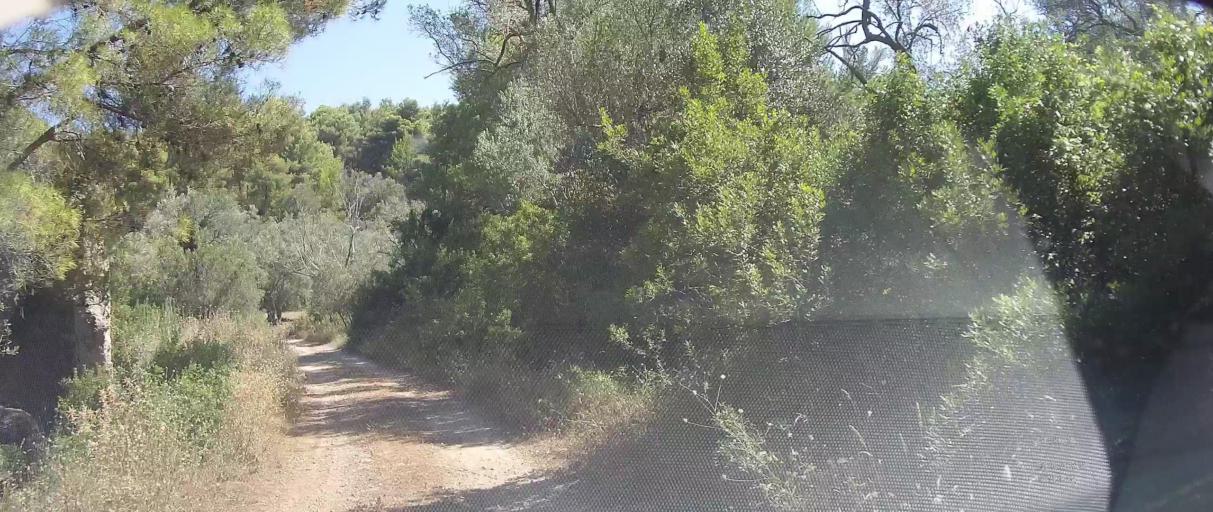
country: HR
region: Dubrovacko-Neretvanska
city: Blato
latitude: 42.7289
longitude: 17.5550
